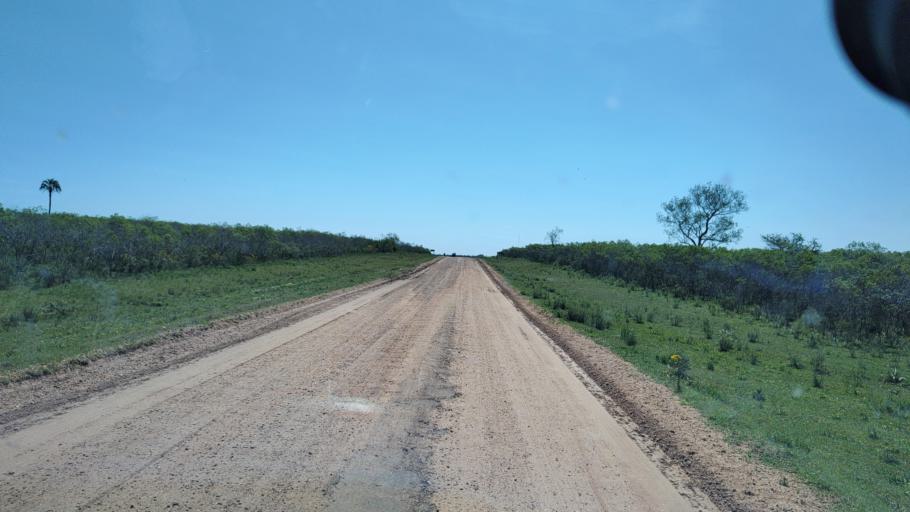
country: AR
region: Entre Rios
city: Ubajay
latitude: -31.8675
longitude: -58.2502
